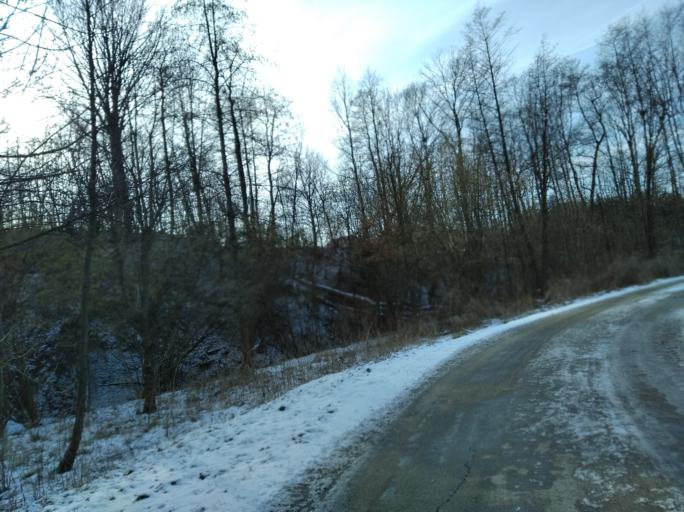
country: PL
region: Subcarpathian Voivodeship
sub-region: Powiat krosnienski
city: Korczyna
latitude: 49.7697
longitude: 21.7912
